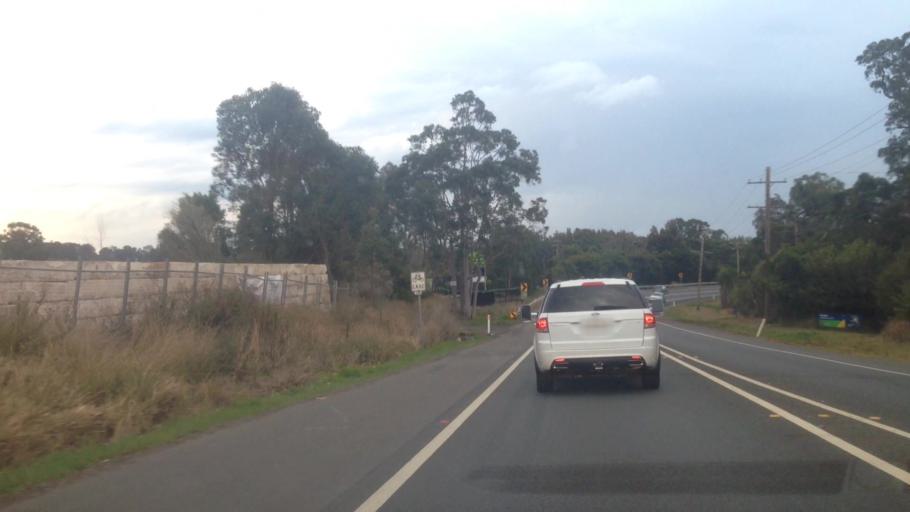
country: AU
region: New South Wales
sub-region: Wyong Shire
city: Tuggerawong
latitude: -33.2638
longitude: 151.4554
